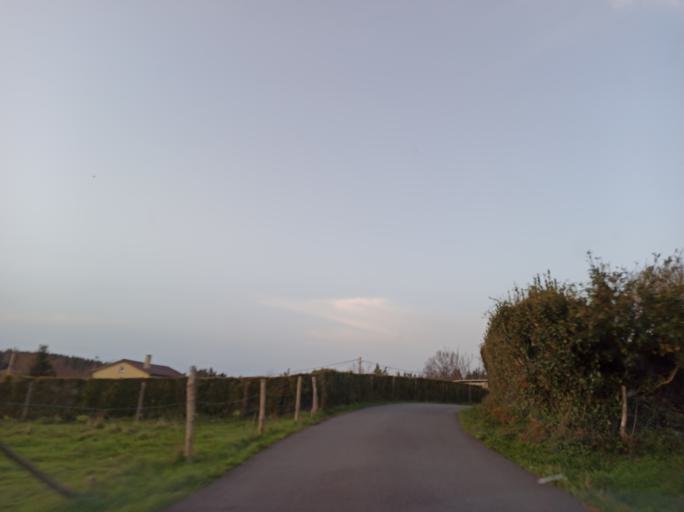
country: ES
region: Galicia
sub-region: Provincia da Coruna
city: Cesuras
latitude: 43.1802
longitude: -8.1451
